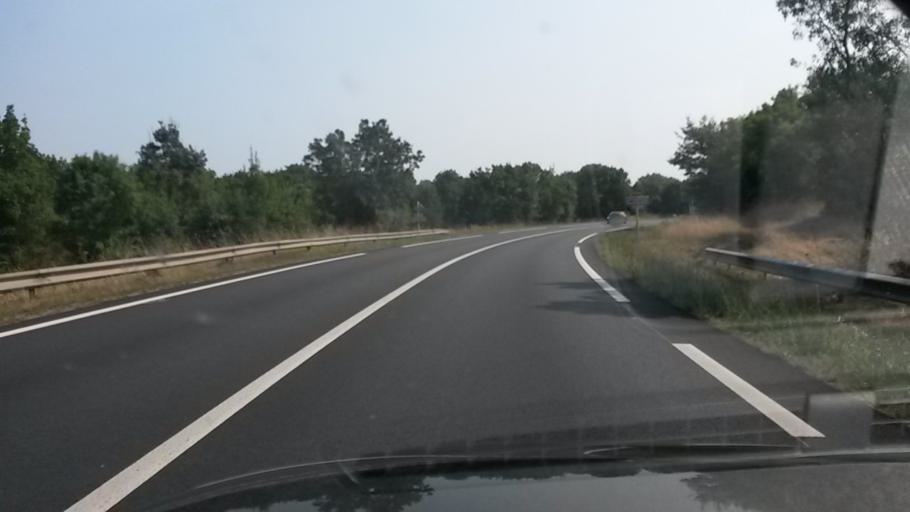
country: FR
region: Pays de la Loire
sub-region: Departement de la Loire-Atlantique
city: Ancenis
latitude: 47.3746
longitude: -1.1673
